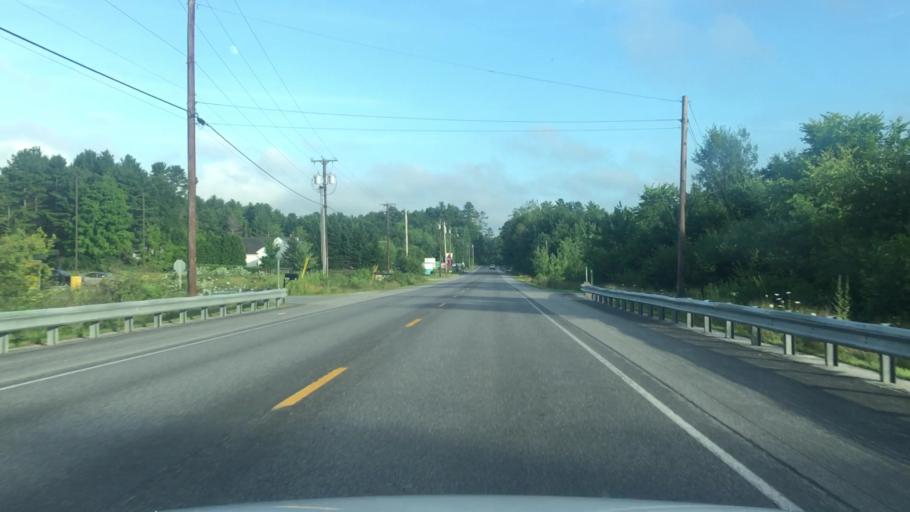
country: US
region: Maine
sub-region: Cumberland County
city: North Windham
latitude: 43.7976
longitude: -70.4016
